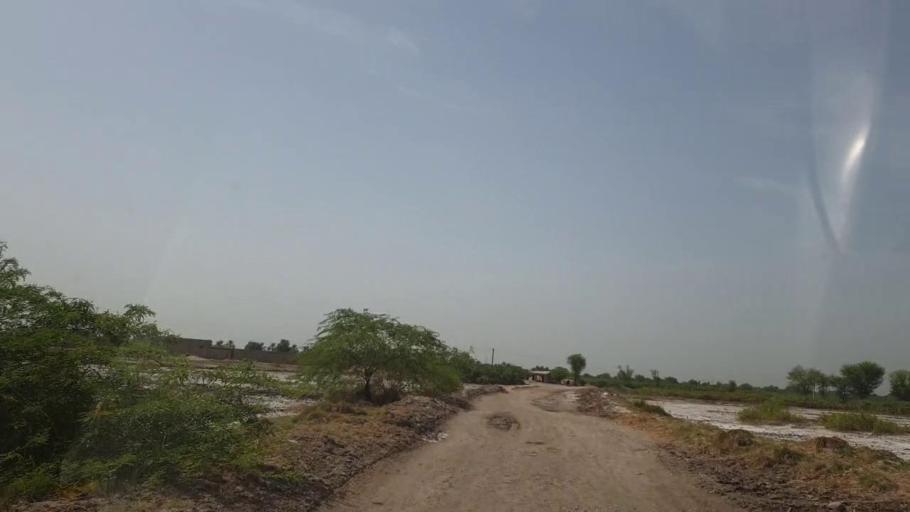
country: PK
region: Sindh
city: Gambat
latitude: 27.3799
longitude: 68.5833
